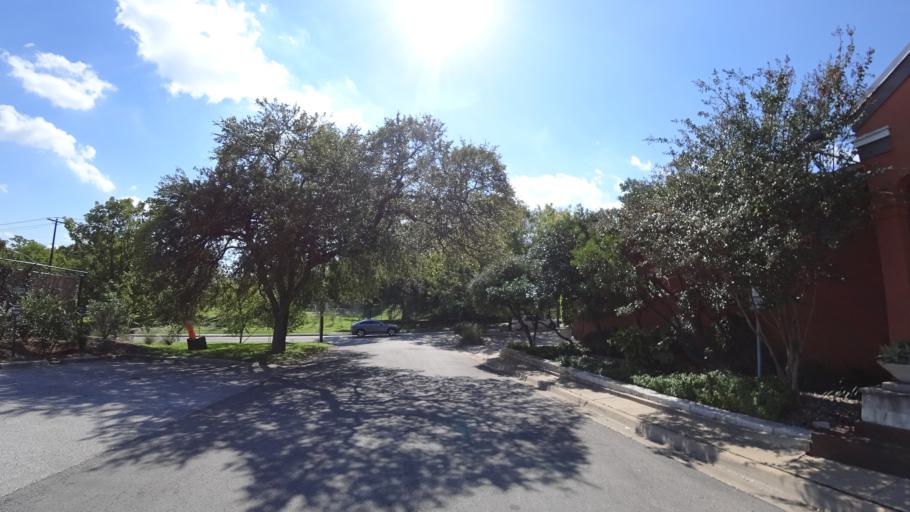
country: US
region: Texas
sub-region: Travis County
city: Austin
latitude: 30.3056
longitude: -97.7497
